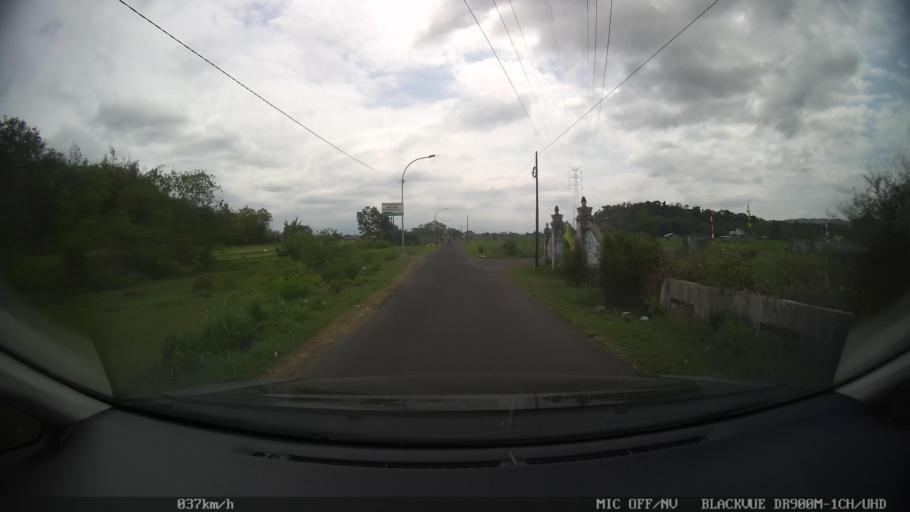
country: ID
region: Daerah Istimewa Yogyakarta
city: Depok
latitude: -7.8163
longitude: 110.4650
